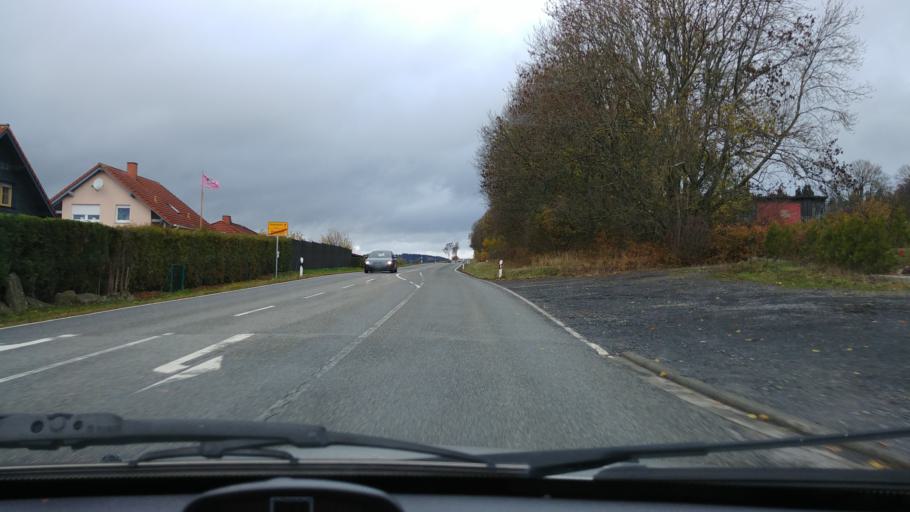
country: DE
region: Hesse
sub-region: Regierungsbezirk Giessen
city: Driedorf
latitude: 50.6381
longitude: 8.1849
